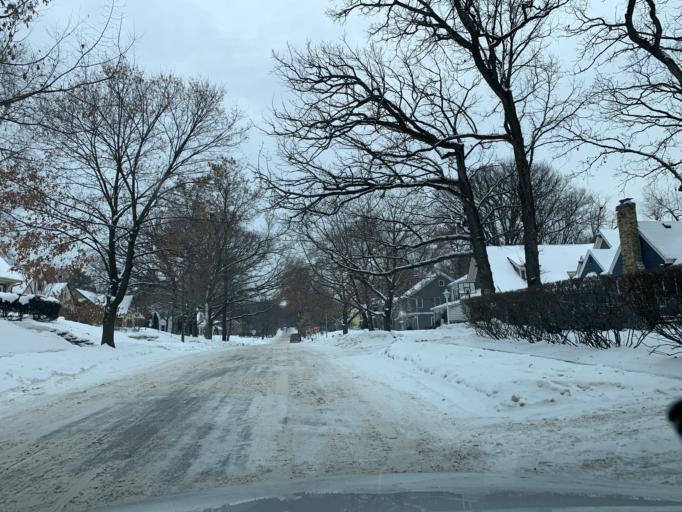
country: US
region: Minnesota
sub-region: Hennepin County
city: Saint Louis Park
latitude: 44.9223
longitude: -93.3446
